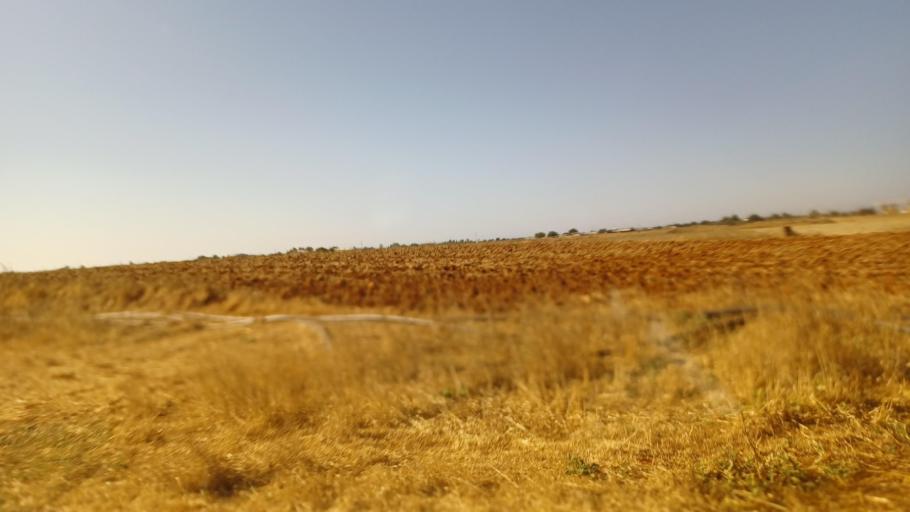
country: CY
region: Ammochostos
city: Avgorou
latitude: 35.0164
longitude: 33.8474
